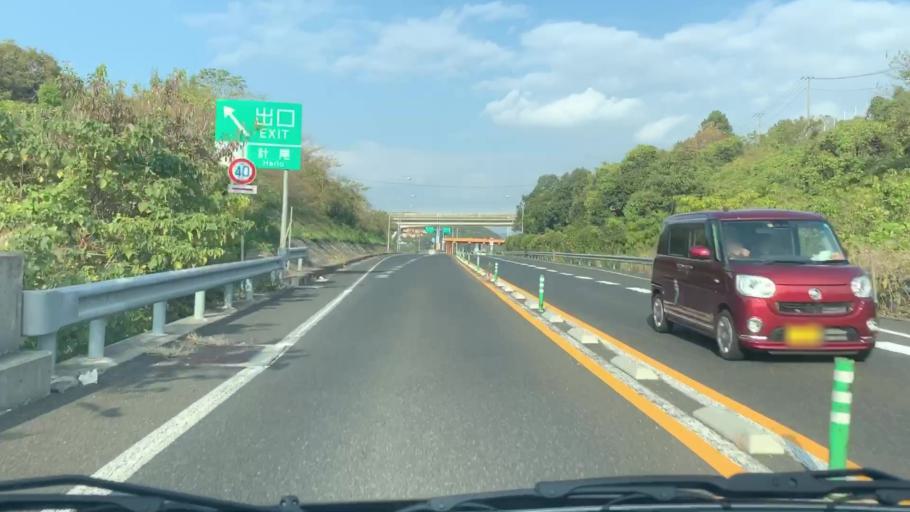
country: JP
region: Nagasaki
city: Sasebo
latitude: 33.0627
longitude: 129.7601
